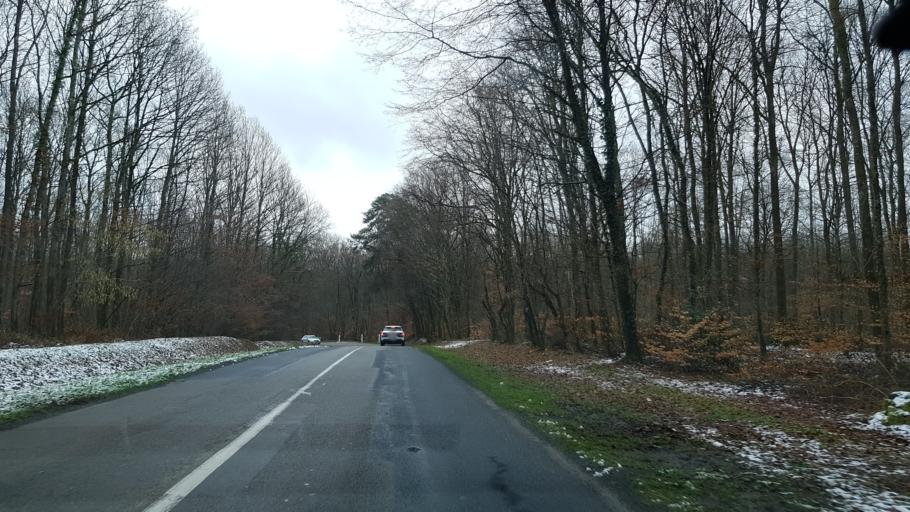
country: FR
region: Rhone-Alpes
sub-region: Departement de l'Ain
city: Peronnas
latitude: 46.1759
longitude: 5.2359
